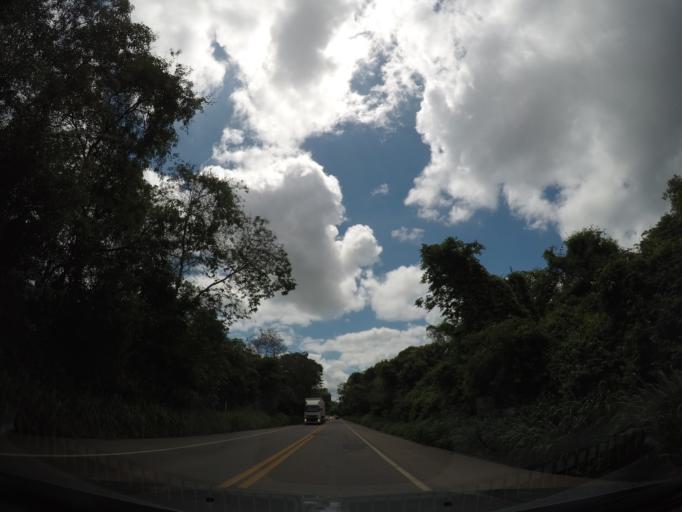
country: BR
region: Bahia
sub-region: Iraquara
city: Iraquara
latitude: -12.4787
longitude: -41.3586
